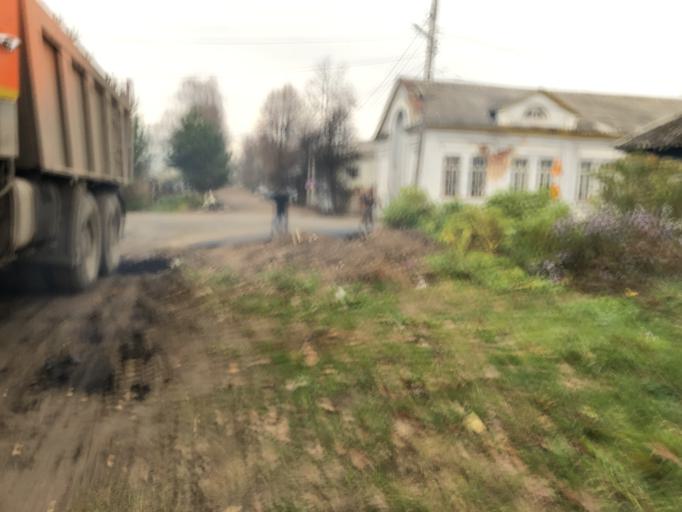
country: RU
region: Tverskaya
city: Rzhev
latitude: 56.2550
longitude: 34.3244
